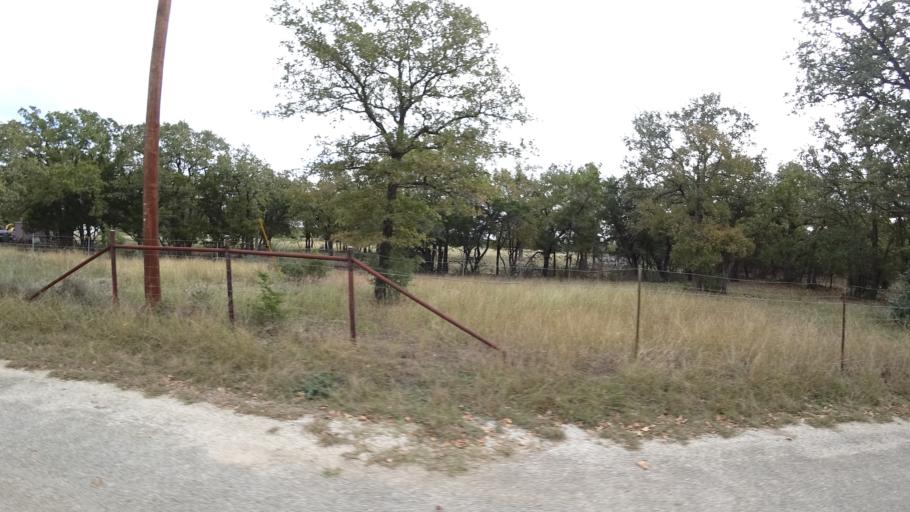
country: US
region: Texas
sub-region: Travis County
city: Shady Hollow
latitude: 30.1379
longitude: -97.8745
